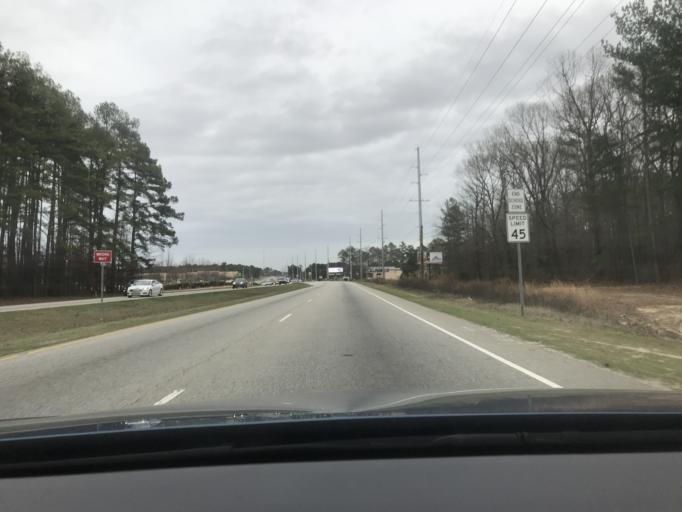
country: US
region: North Carolina
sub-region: Hoke County
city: Rockfish
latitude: 35.0384
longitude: -79.0032
